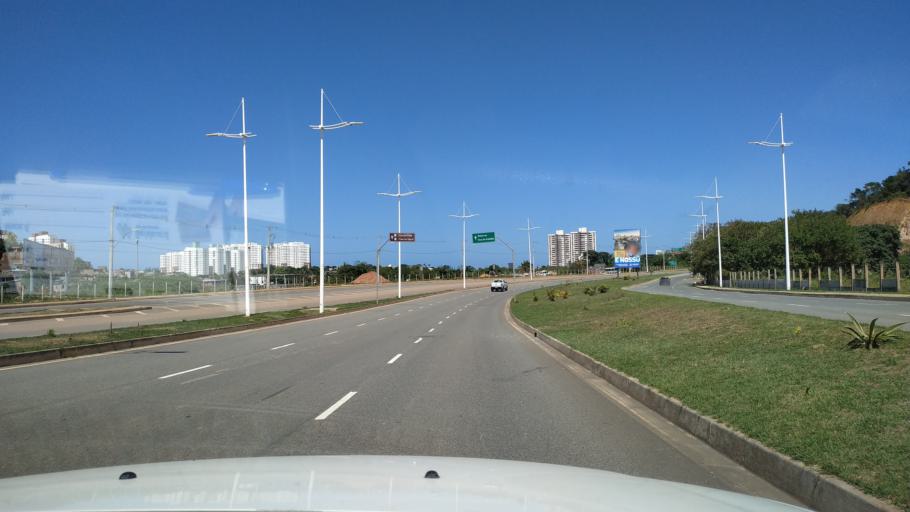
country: BR
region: Bahia
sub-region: Lauro De Freitas
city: Lauro de Freitas
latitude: -12.9297
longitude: -38.3816
